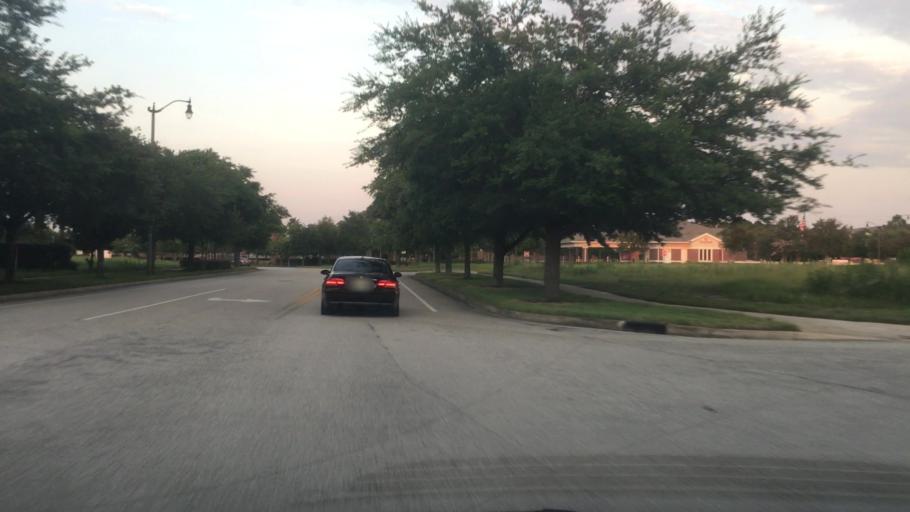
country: US
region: Florida
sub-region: Duval County
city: Jacksonville
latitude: 30.3390
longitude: -81.5474
